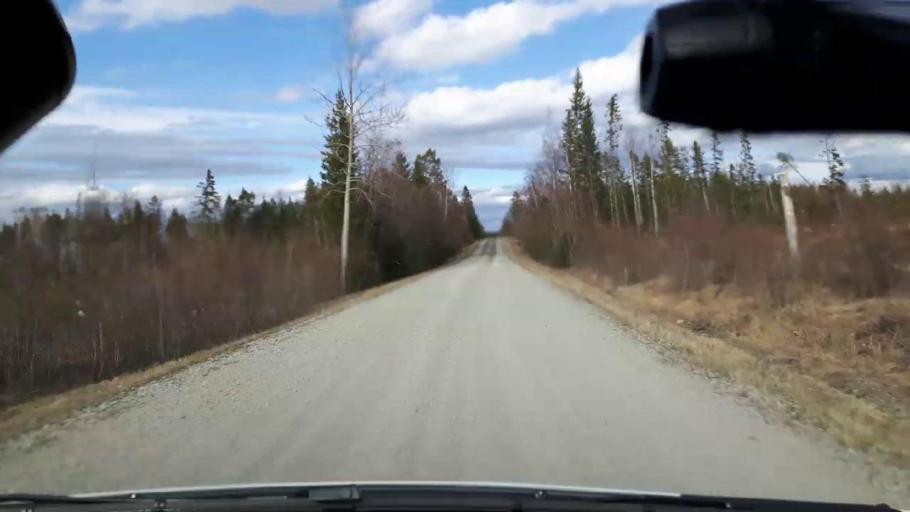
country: SE
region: Jaemtland
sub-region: Bergs Kommun
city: Hoverberg
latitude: 62.7585
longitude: 14.6652
